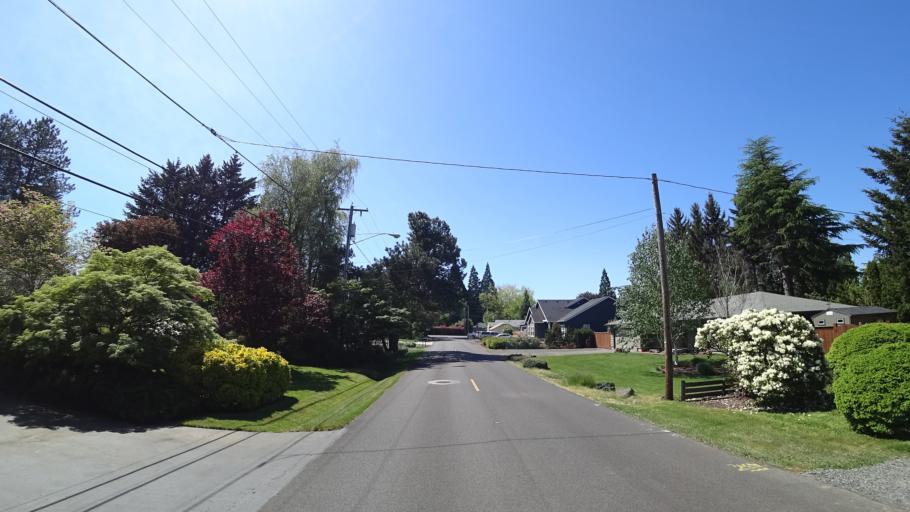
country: US
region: Oregon
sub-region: Washington County
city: Hillsboro
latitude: 45.5122
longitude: -122.9483
